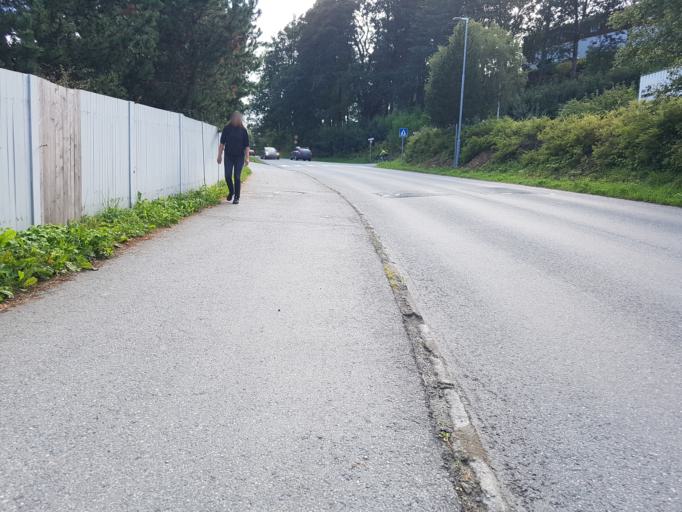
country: NO
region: Sor-Trondelag
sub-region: Trondheim
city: Trondheim
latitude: 63.4307
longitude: 10.4387
